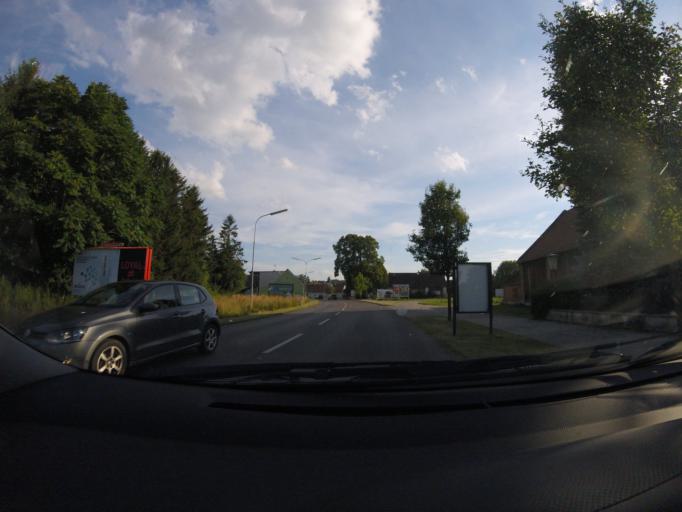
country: AT
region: Lower Austria
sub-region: Politischer Bezirk Wiener Neustadt
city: Zillingdorf
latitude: 47.8608
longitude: 16.3240
